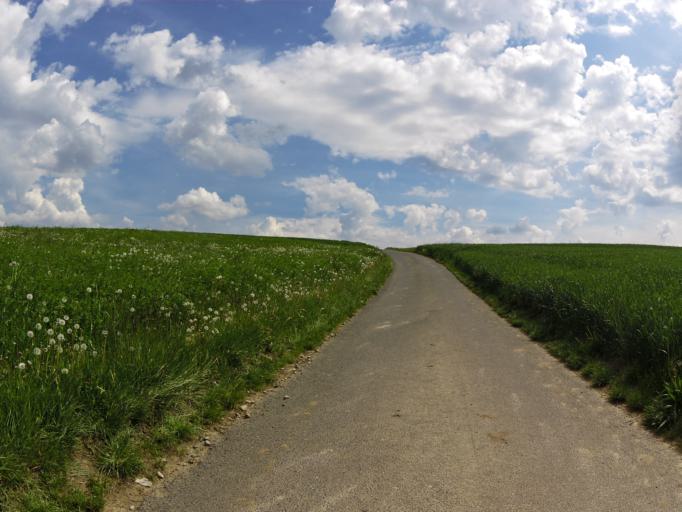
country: DE
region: Bavaria
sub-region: Regierungsbezirk Unterfranken
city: Theilheim
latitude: 49.7389
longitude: 10.0420
